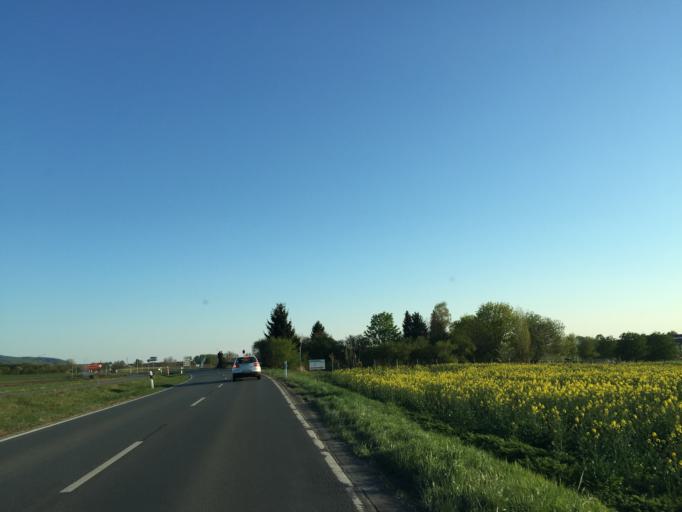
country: DE
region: Hesse
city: Pfungstadt
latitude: 49.7902
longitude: 8.6018
